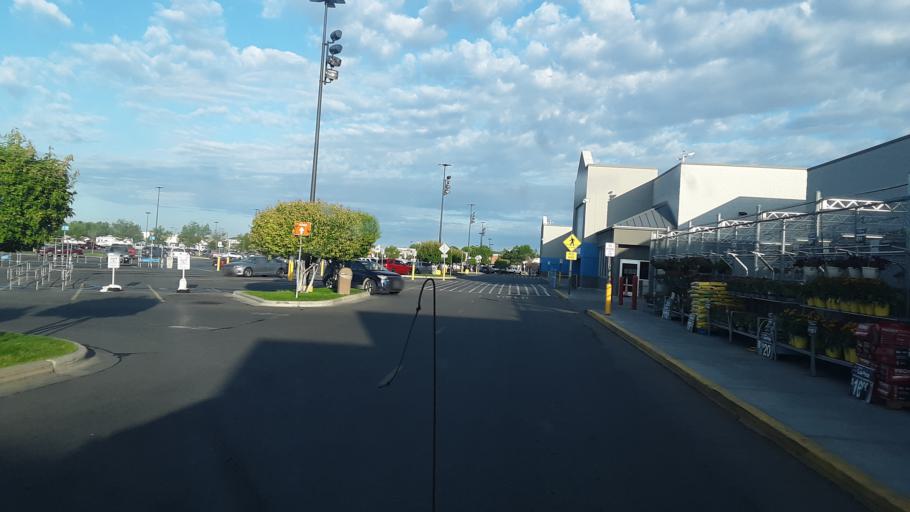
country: US
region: Montana
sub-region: Yellowstone County
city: Billings
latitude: 45.7575
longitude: -108.5783
